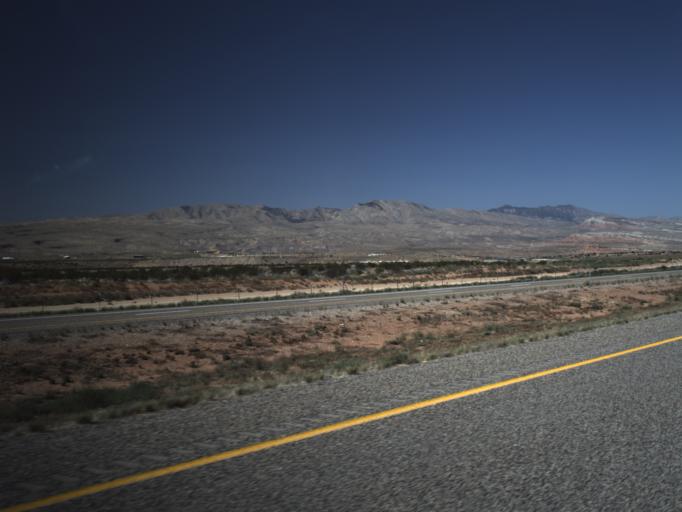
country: US
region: Utah
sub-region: Washington County
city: Saint George
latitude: 37.0137
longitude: -113.5926
